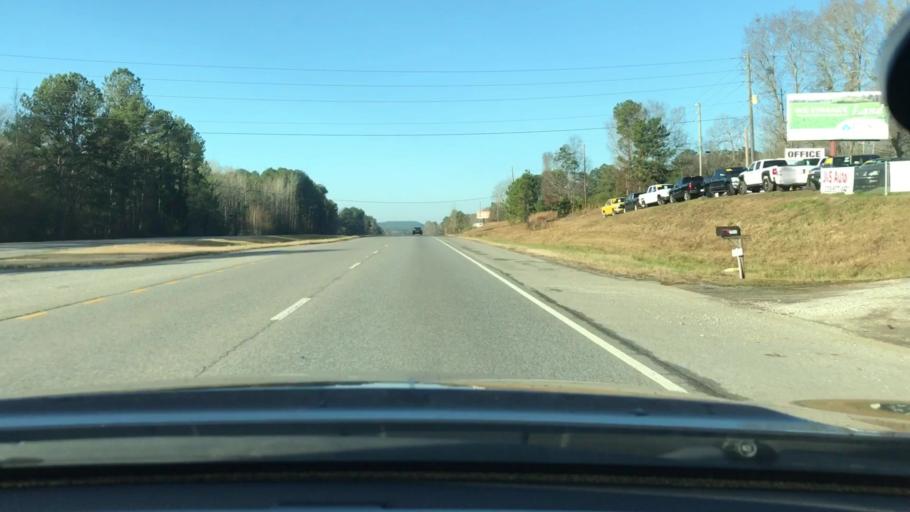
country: US
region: Alabama
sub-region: Shelby County
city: Westover
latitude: 33.3498
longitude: -86.5482
